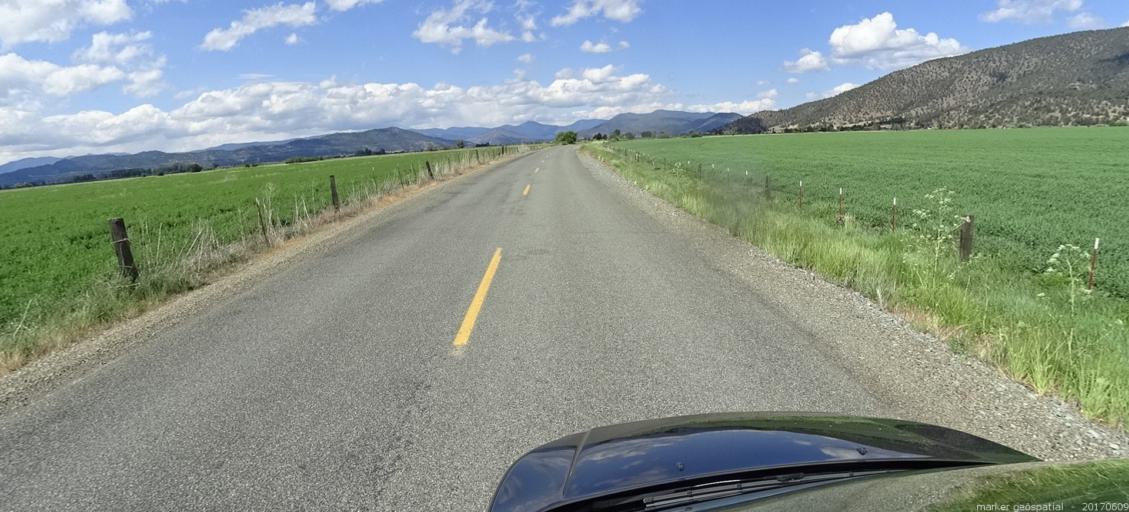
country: US
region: California
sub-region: Siskiyou County
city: Yreka
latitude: 41.5006
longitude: -122.8587
